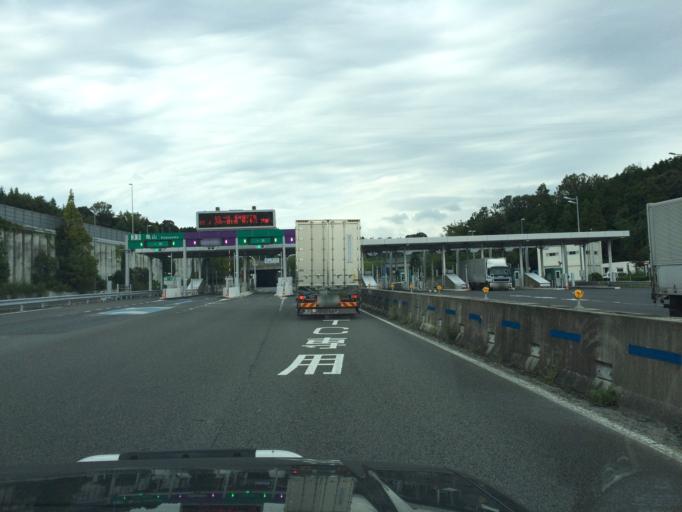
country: JP
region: Mie
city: Kameyama
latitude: 34.8604
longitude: 136.4133
